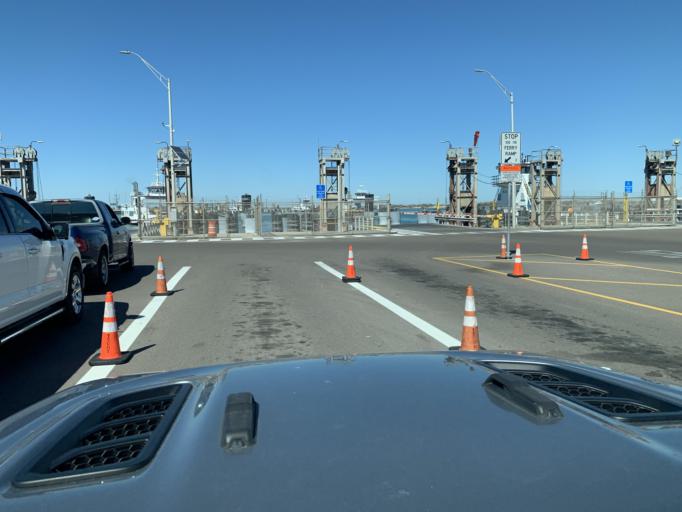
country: US
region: Texas
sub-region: Nueces County
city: Port Aransas
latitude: 27.8394
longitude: -97.0692
